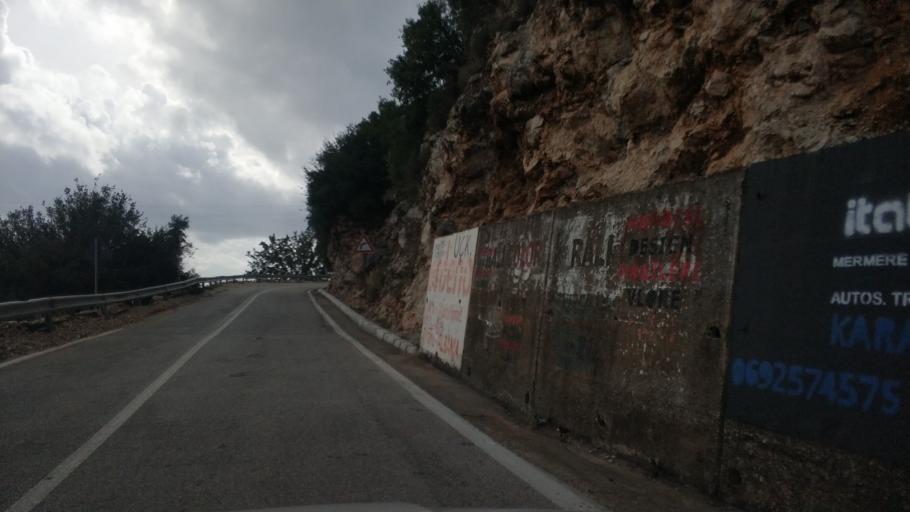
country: AL
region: Vlore
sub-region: Rrethi i Vlores
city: Vranisht
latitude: 40.1751
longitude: 19.6066
